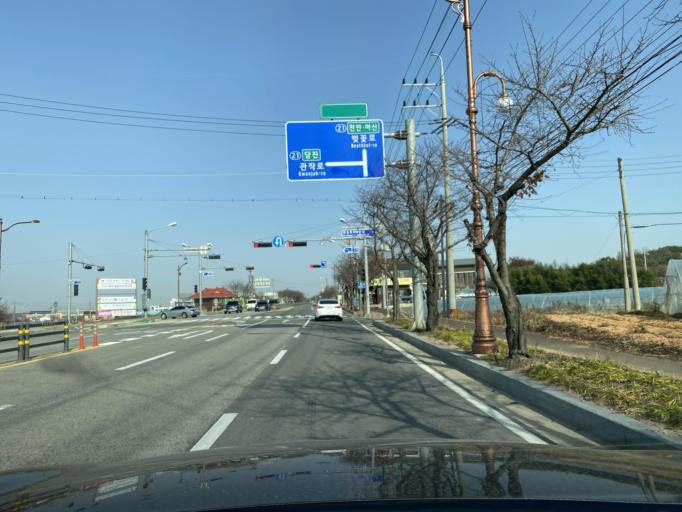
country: KR
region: Chungcheongnam-do
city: Yesan
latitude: 36.7074
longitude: 126.8398
